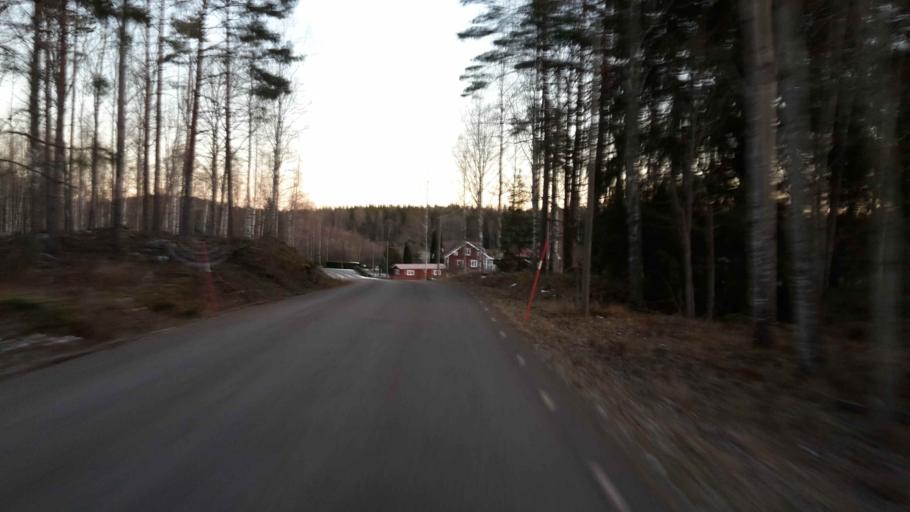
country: SE
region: OEstergoetland
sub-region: Atvidabergs Kommun
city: Atvidaberg
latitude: 58.2447
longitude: 16.0971
